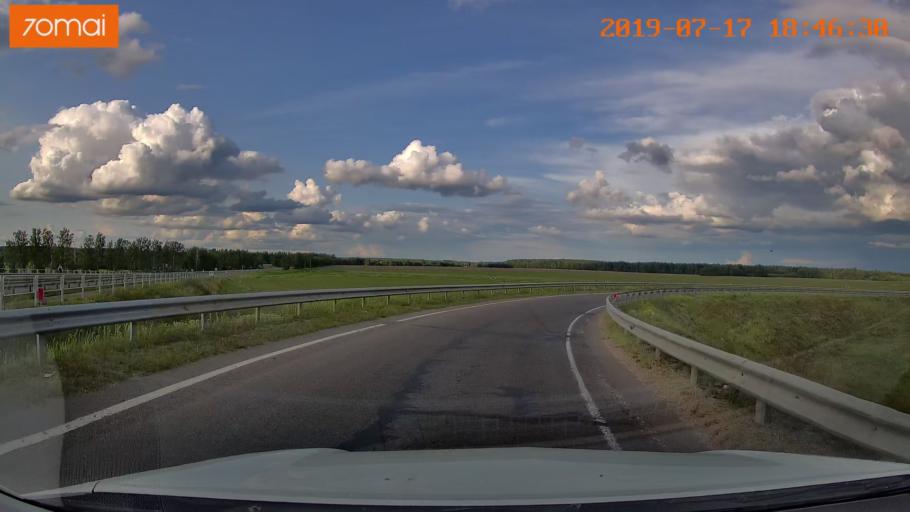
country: BY
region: Mogilev
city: Asipovichy
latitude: 53.3368
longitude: 28.6658
